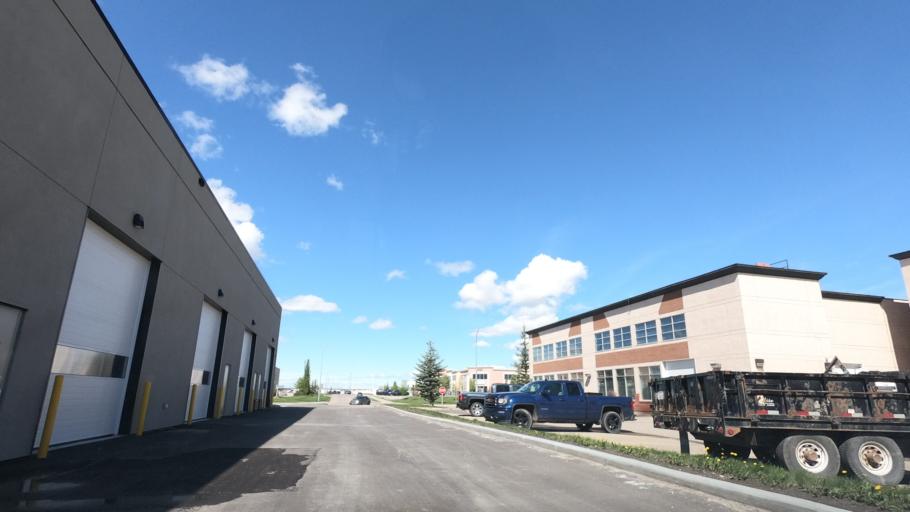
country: CA
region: Alberta
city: Airdrie
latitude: 51.2617
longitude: -113.9939
